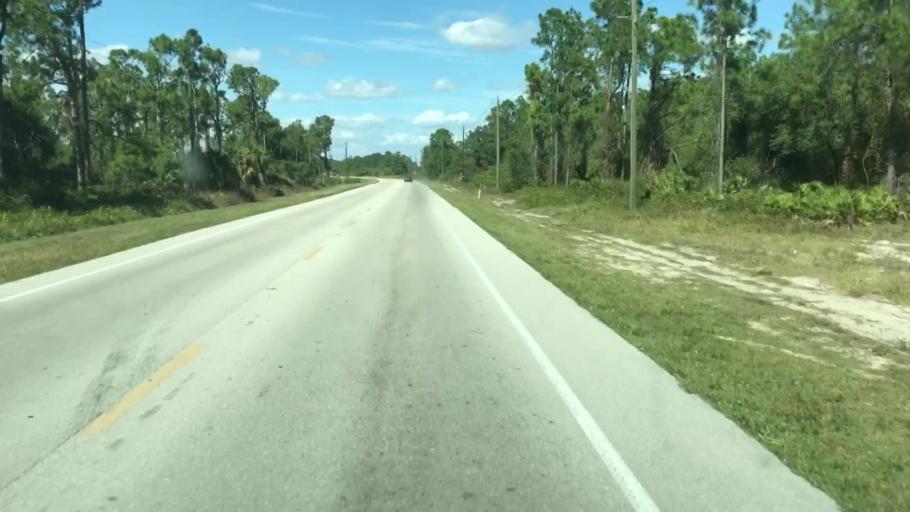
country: US
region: Florida
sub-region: Lee County
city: Alva
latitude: 26.6857
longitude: -81.5986
